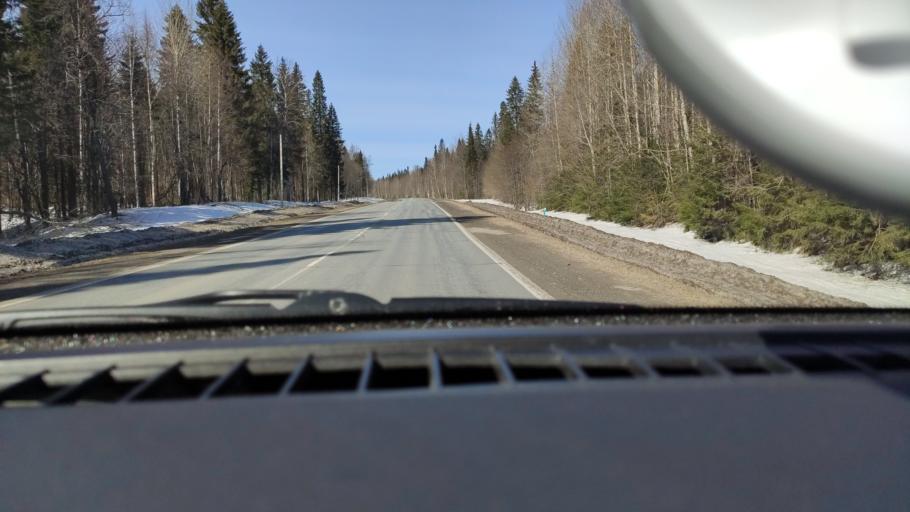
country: RU
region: Perm
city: Perm
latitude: 58.2043
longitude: 56.2005
